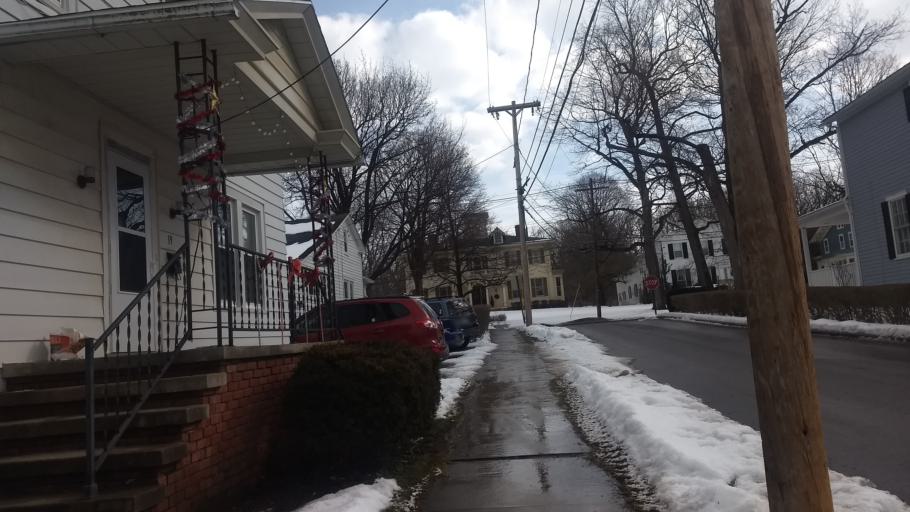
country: US
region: New York
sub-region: Livingston County
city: Geneseo
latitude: 42.7974
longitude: -77.8147
